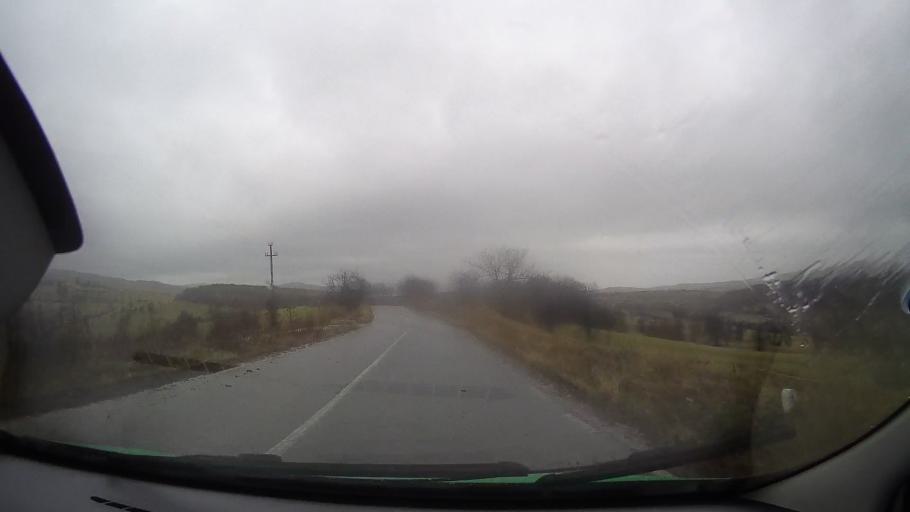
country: RO
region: Mures
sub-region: Comuna Vatava
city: Vatava
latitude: 46.9552
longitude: 24.7478
